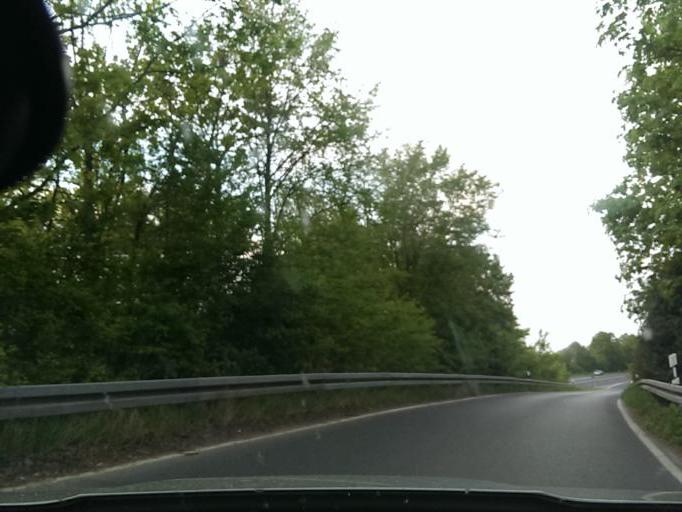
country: DE
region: Lower Saxony
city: Banteln
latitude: 52.0812
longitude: 9.7435
